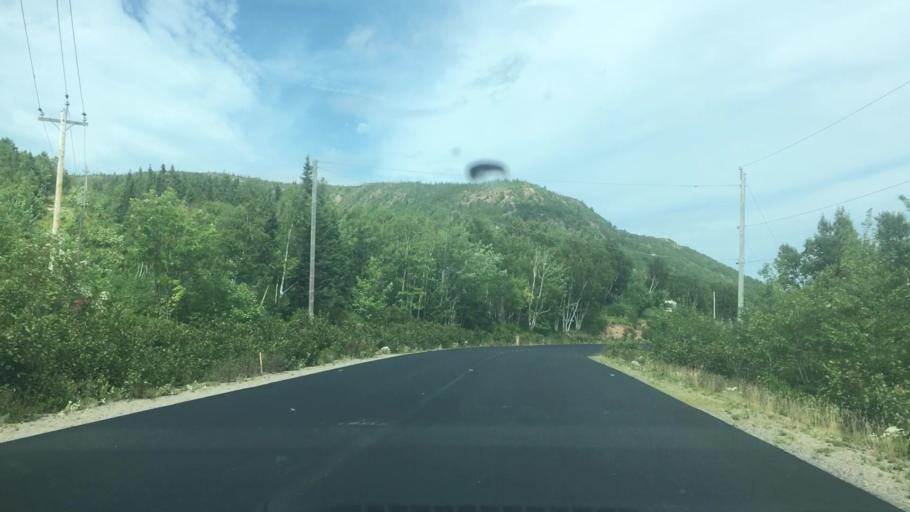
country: CA
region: Nova Scotia
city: Sydney Mines
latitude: 46.5752
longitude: -60.3914
